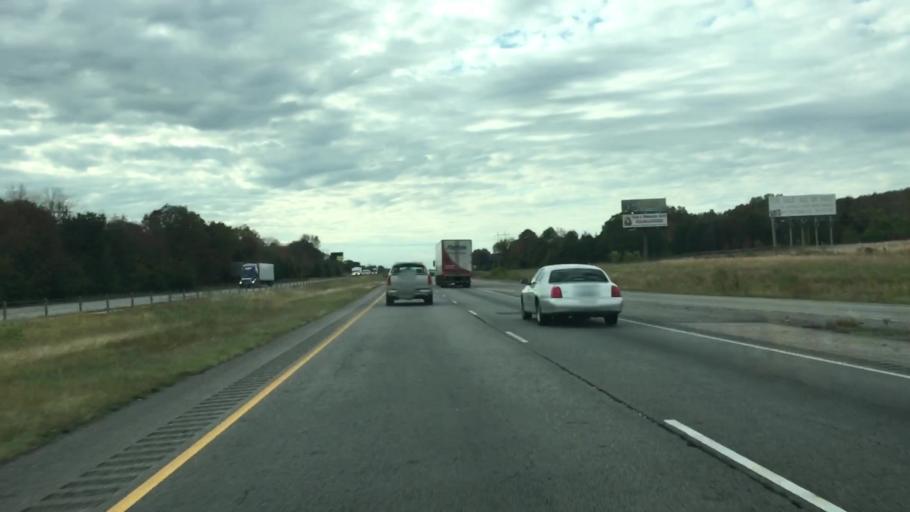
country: US
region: Arkansas
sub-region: Conway County
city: Morrilton
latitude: 35.1630
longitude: -92.6446
